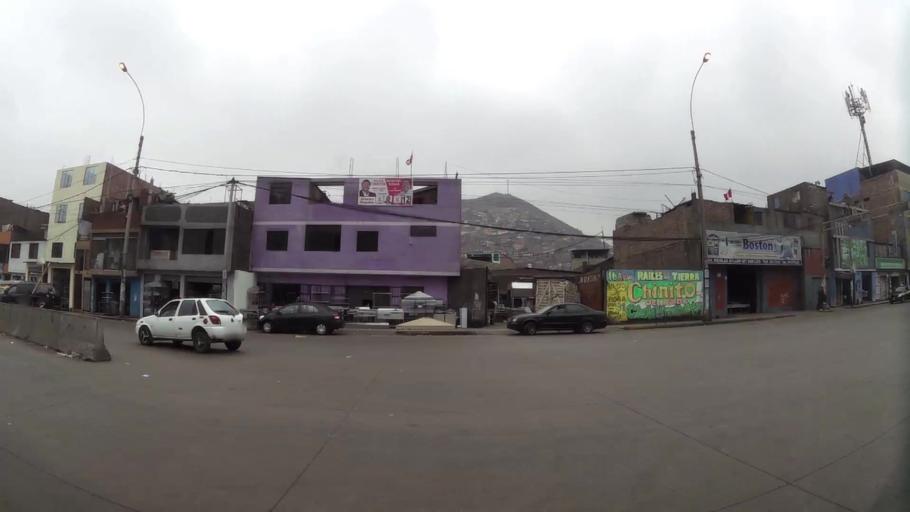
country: PE
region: Lima
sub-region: Lima
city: San Luis
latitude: -12.0635
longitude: -76.9999
